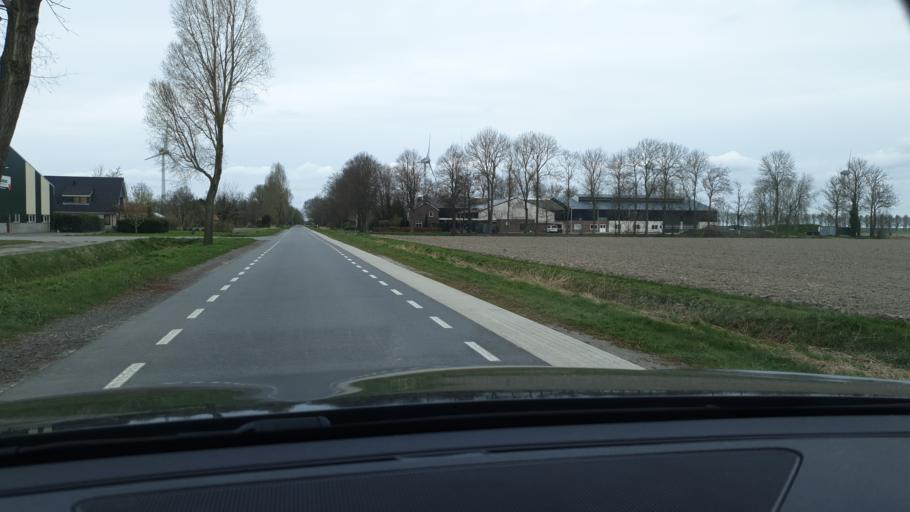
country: NL
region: Friesland
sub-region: Gemeente Lemsterland
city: Lemmer
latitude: 52.7764
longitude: 5.6349
